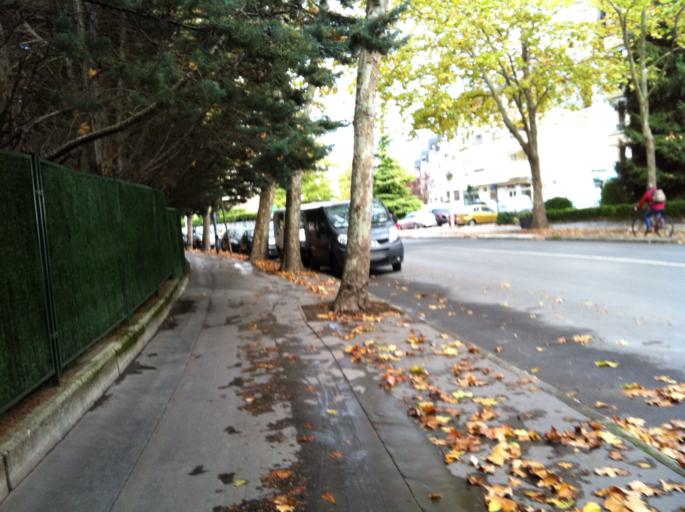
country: ES
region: Basque Country
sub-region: Provincia de Alava
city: Gasteiz / Vitoria
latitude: 42.8388
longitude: -2.6835
